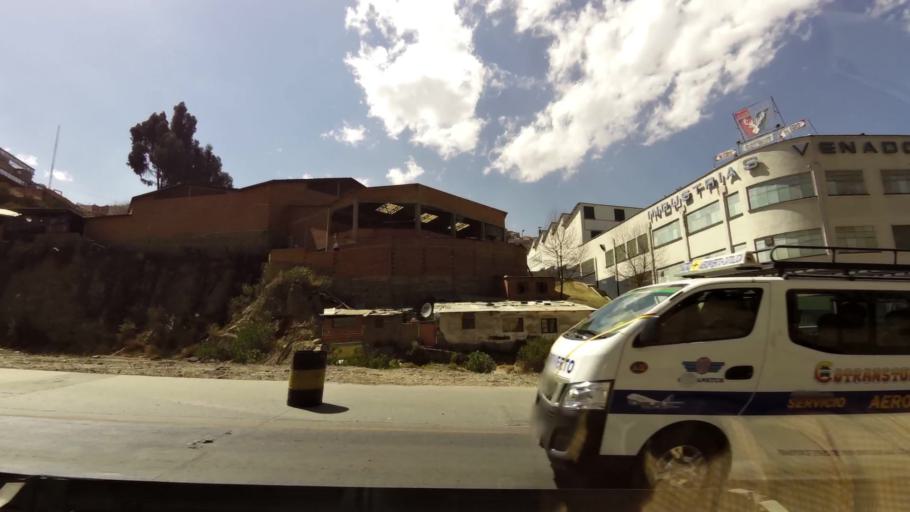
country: BO
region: La Paz
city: La Paz
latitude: -16.4862
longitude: -68.1453
